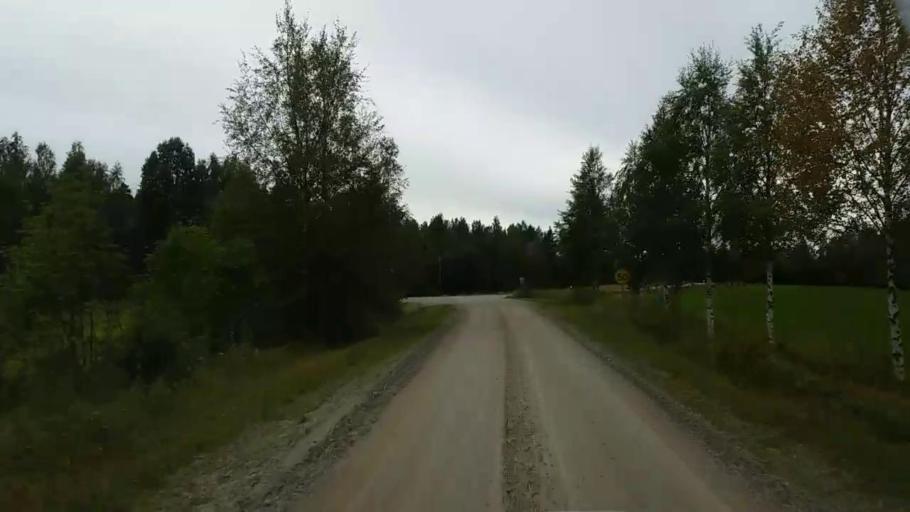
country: SE
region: Gaevleborg
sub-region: Ljusdals Kommun
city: Farila
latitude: 61.8075
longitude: 15.8601
